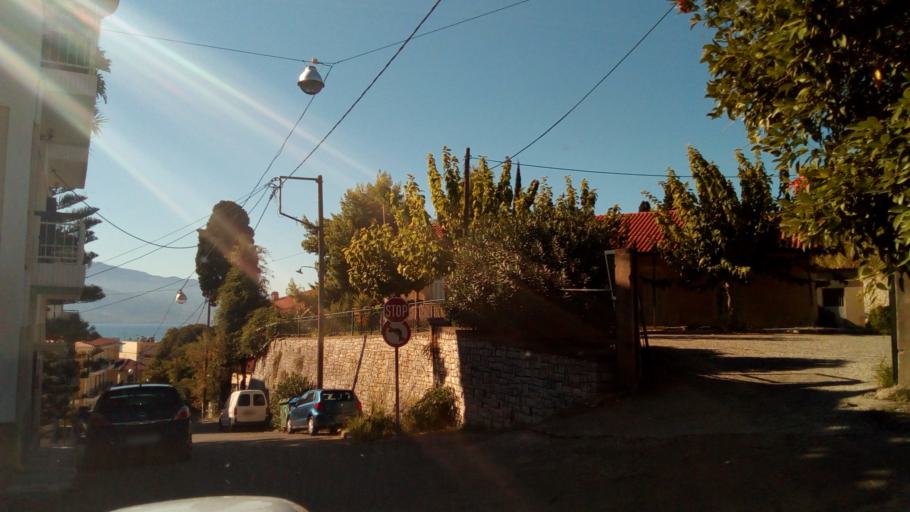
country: GR
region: West Greece
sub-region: Nomos Aitolias kai Akarnanias
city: Nafpaktos
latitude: 38.3958
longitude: 21.8305
